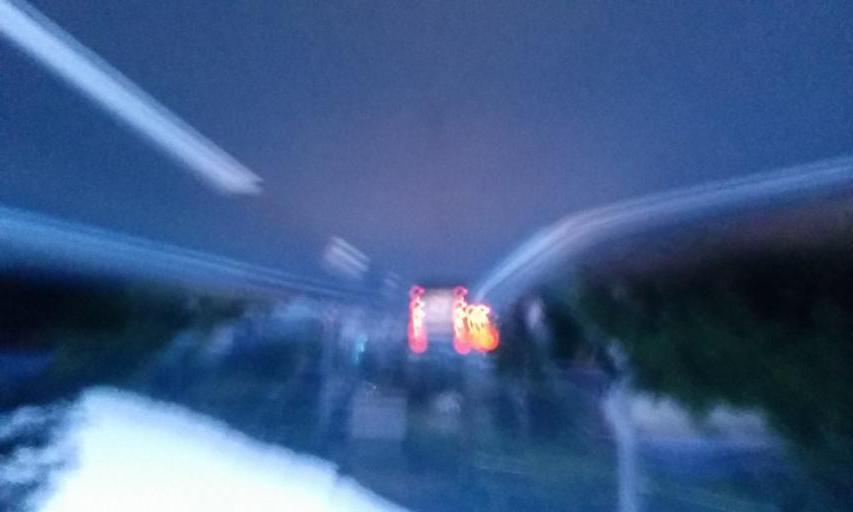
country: JP
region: Ehime
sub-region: Nishiuwa-gun
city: Ikata-cho
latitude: 33.5073
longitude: 132.3970
